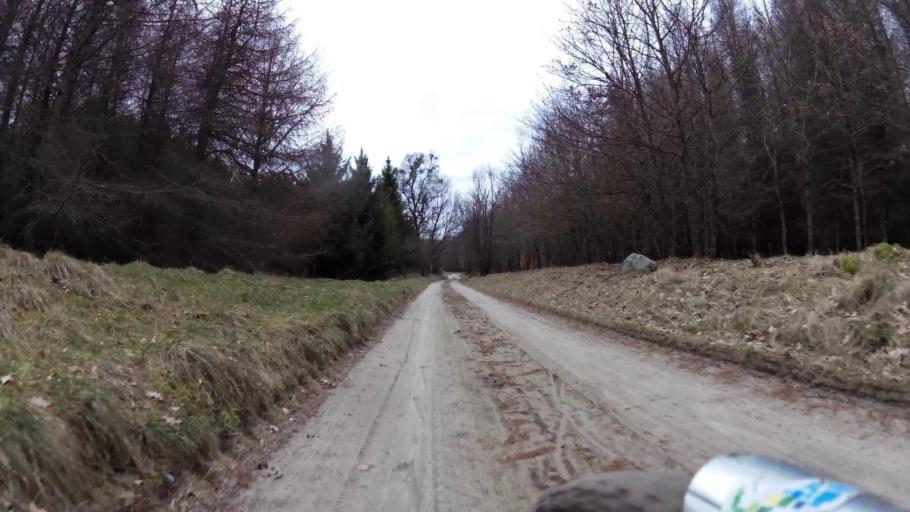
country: PL
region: Pomeranian Voivodeship
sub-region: Powiat bytowski
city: Trzebielino
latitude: 54.1127
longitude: 17.1294
